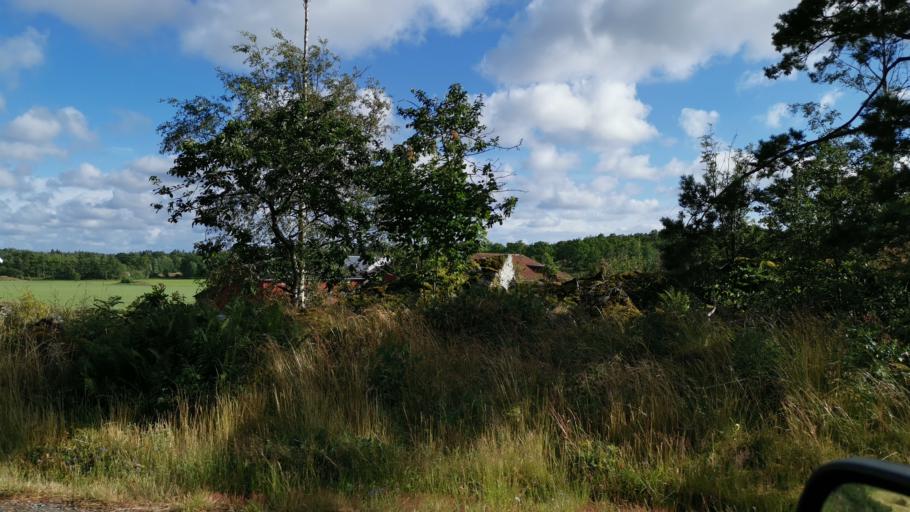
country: SE
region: Vaestra Goetaland
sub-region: Orust
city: Henan
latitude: 58.1612
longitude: 11.6178
